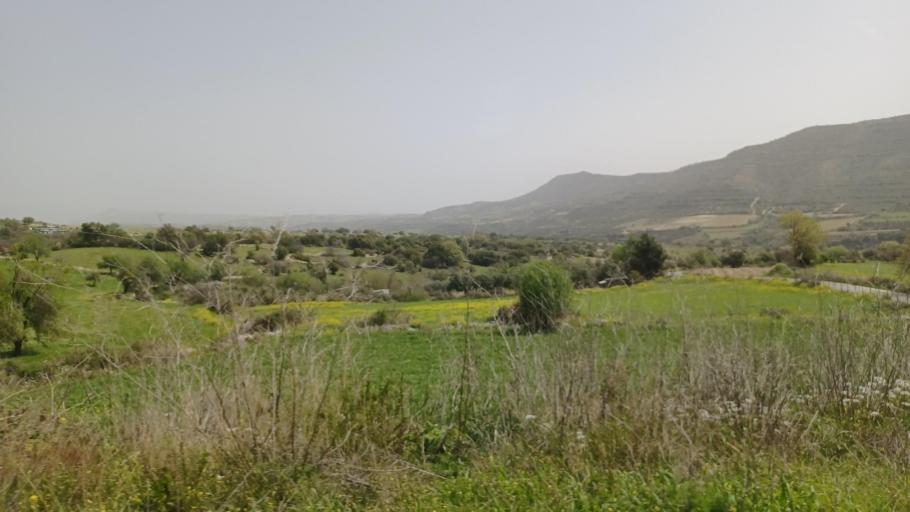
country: CY
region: Limassol
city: Pachna
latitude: 34.7786
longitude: 32.7436
